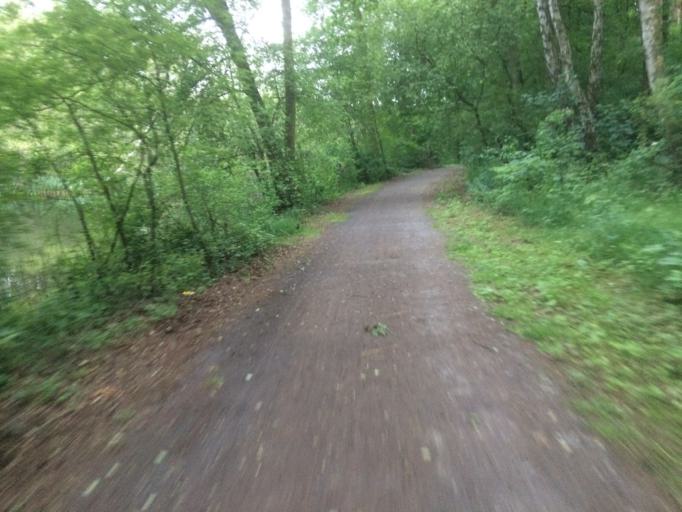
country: PL
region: Lubusz
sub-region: Powiat swiebodzinski
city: Skape
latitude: 52.2128
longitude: 15.4191
